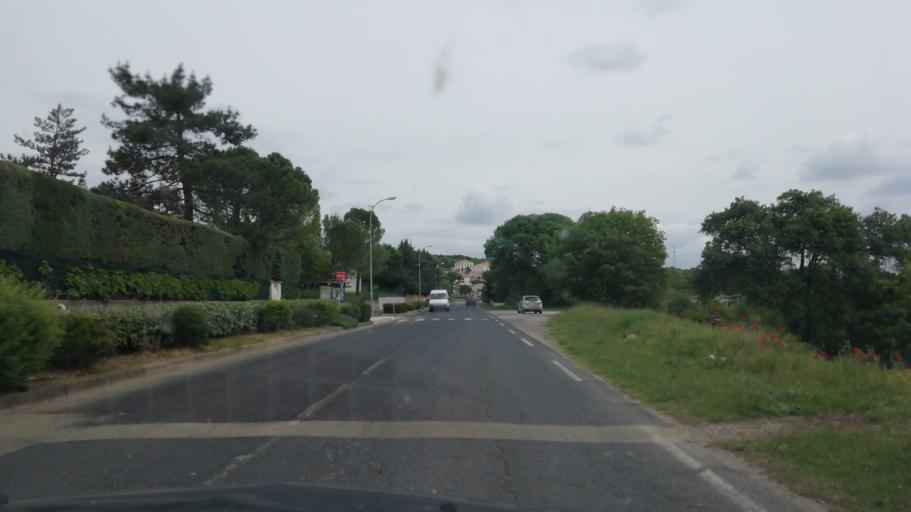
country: FR
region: Languedoc-Roussillon
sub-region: Departement de l'Herault
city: Saint-Martin-de-Londres
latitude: 43.7950
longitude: 3.7337
